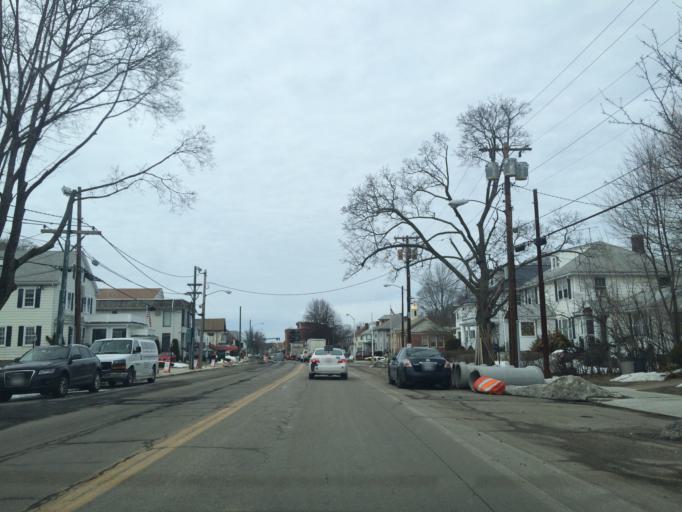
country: US
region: Massachusetts
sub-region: Middlesex County
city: Watertown
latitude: 42.3793
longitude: -71.1721
